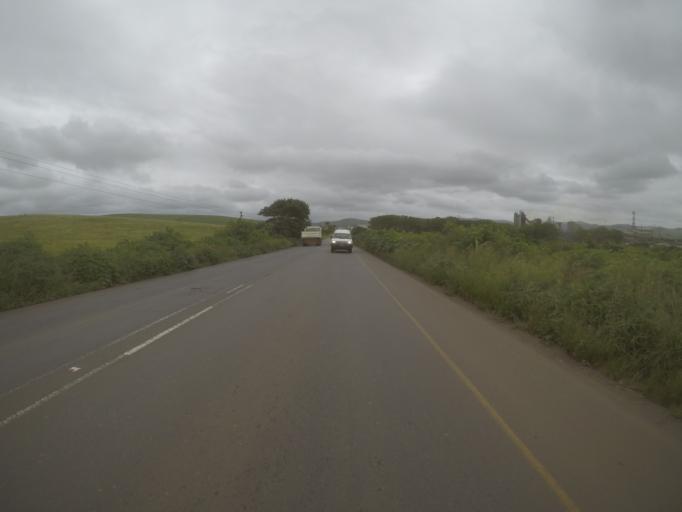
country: ZA
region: KwaZulu-Natal
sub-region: uThungulu District Municipality
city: Empangeni
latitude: -28.7304
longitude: 31.8723
